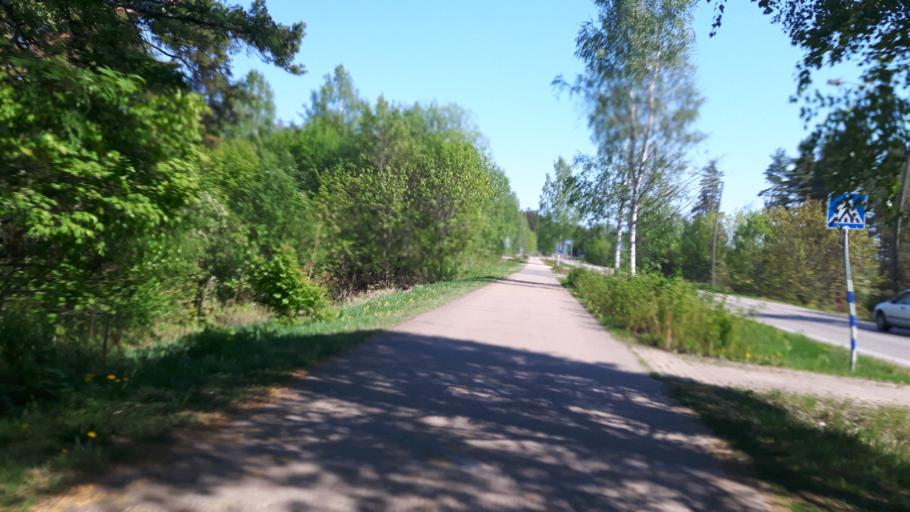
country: FI
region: Kymenlaakso
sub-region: Kotka-Hamina
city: Broby
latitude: 60.4949
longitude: 26.7230
